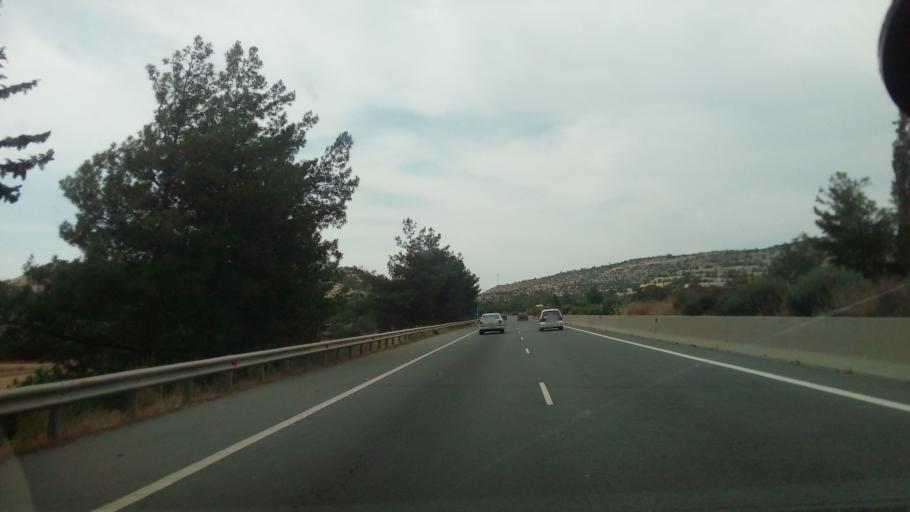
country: CY
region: Larnaka
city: Aradippou
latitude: 34.9758
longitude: 33.5347
